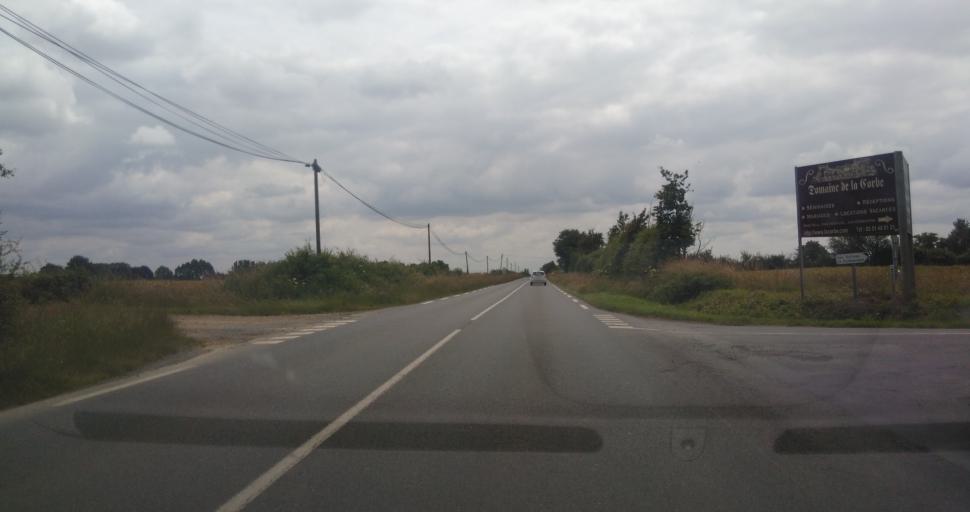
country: FR
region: Pays de la Loire
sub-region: Departement de la Vendee
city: Bournezeau
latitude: 46.6217
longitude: -1.1557
